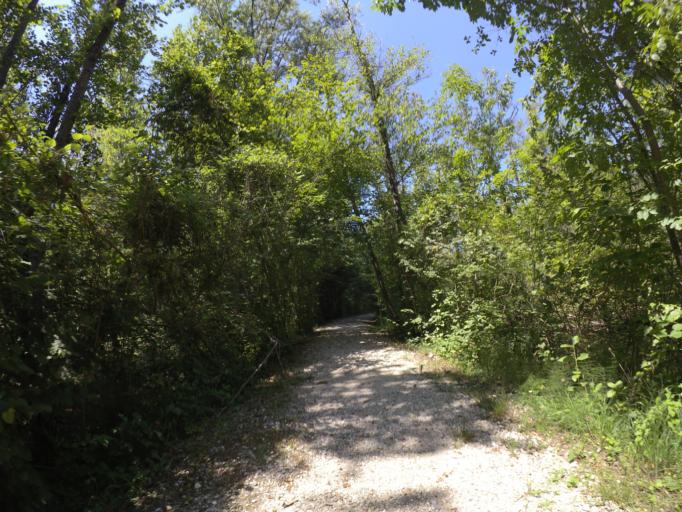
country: IT
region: Friuli Venezia Giulia
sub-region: Provincia di Udine
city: Bertiolo
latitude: 45.9159
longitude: 13.0760
